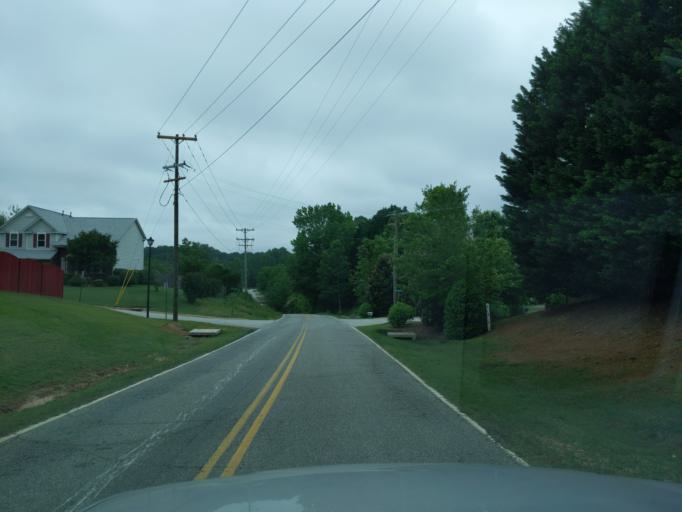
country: US
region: South Carolina
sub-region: Greenville County
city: Five Forks
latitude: 34.8542
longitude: -82.2112
